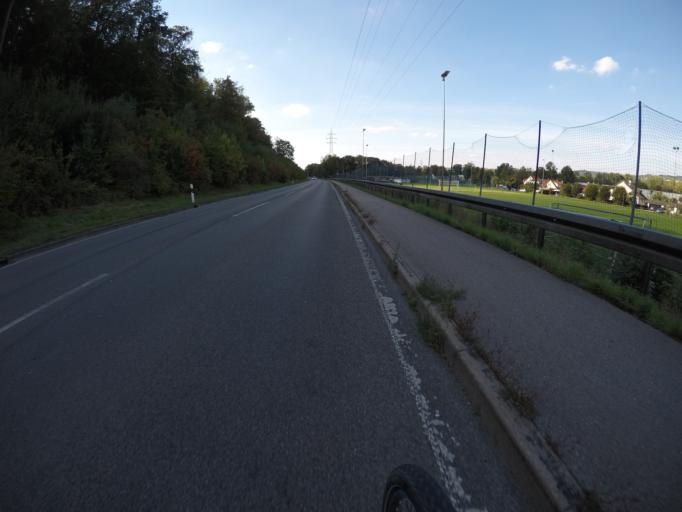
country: DE
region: Baden-Wuerttemberg
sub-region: Regierungsbezirk Stuttgart
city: Esslingen
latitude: 48.7229
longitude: 9.3274
